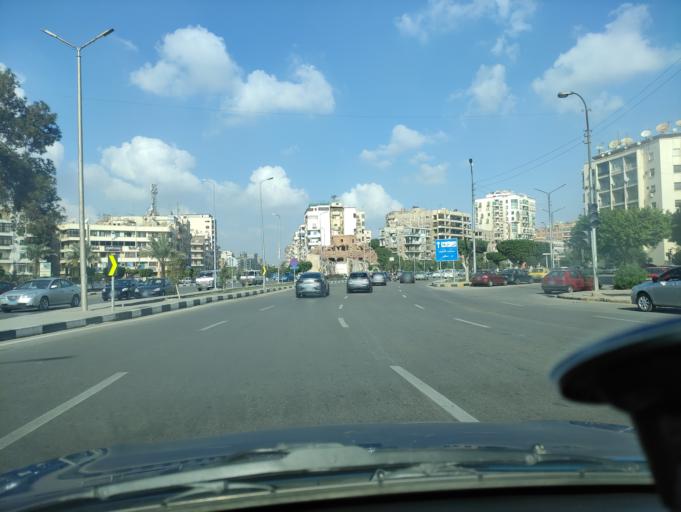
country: EG
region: Muhafazat al Qahirah
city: Cairo
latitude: 30.0995
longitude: 31.3430
